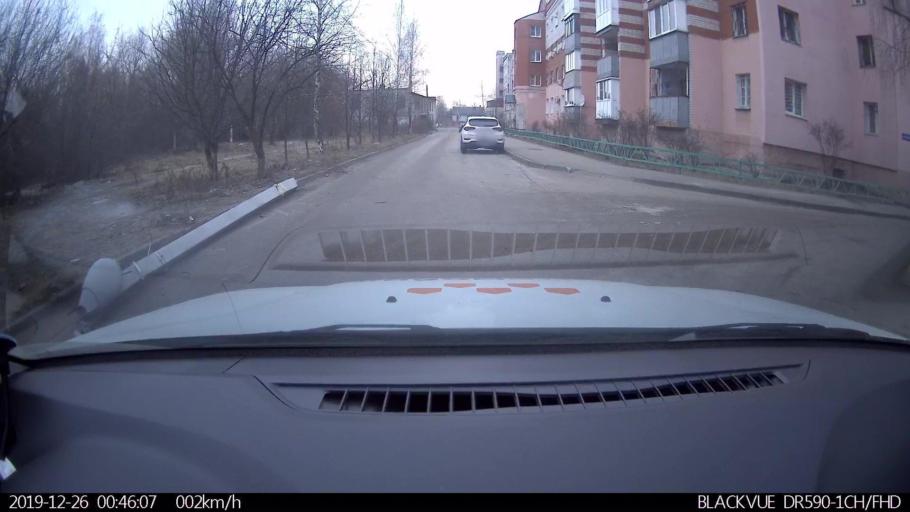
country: RU
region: Nizjnij Novgorod
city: Nizhniy Novgorod
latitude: 56.3014
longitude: 43.8823
